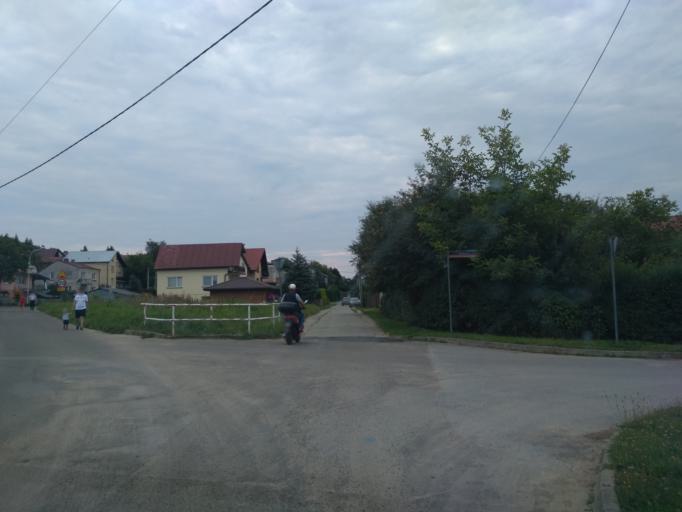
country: PL
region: Subcarpathian Voivodeship
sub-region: Powiat sanocki
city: Sanok
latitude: 49.5699
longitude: 22.1677
